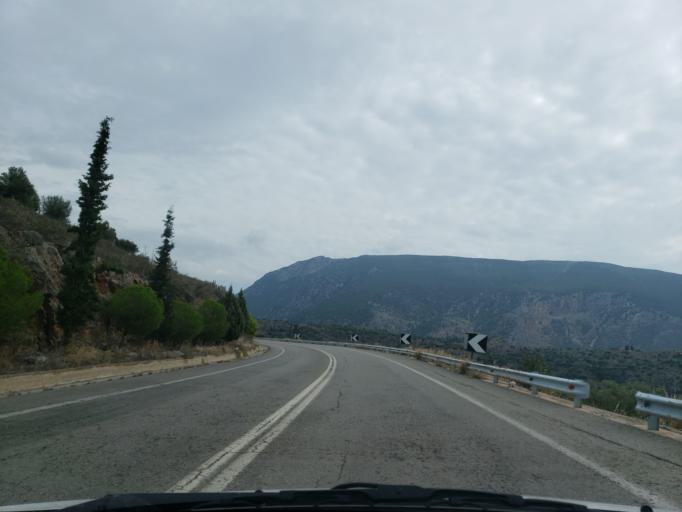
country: GR
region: Central Greece
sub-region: Nomos Fokidos
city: Delphi
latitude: 38.4722
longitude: 22.4576
